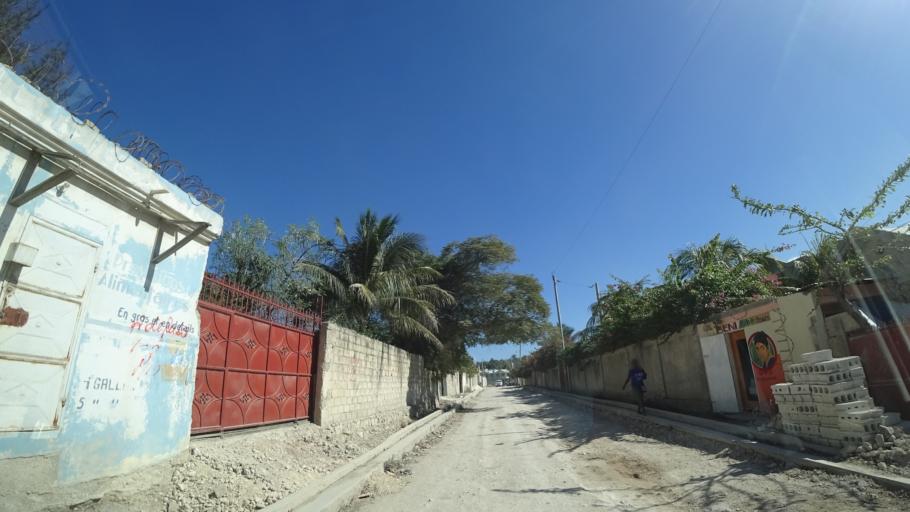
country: HT
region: Ouest
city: Delmas 73
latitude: 18.5562
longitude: -72.2851
